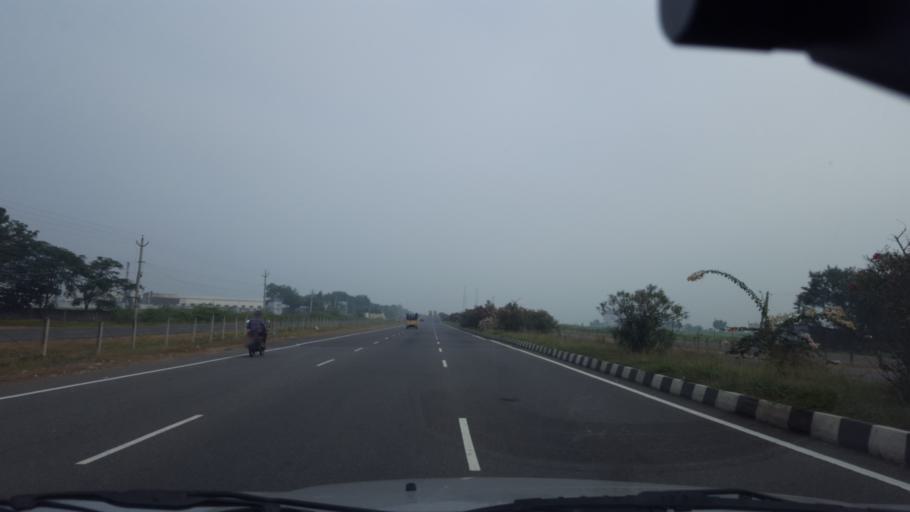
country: IN
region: Andhra Pradesh
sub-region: Guntur
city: Chilakalurupet
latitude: 16.0405
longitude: 80.1359
